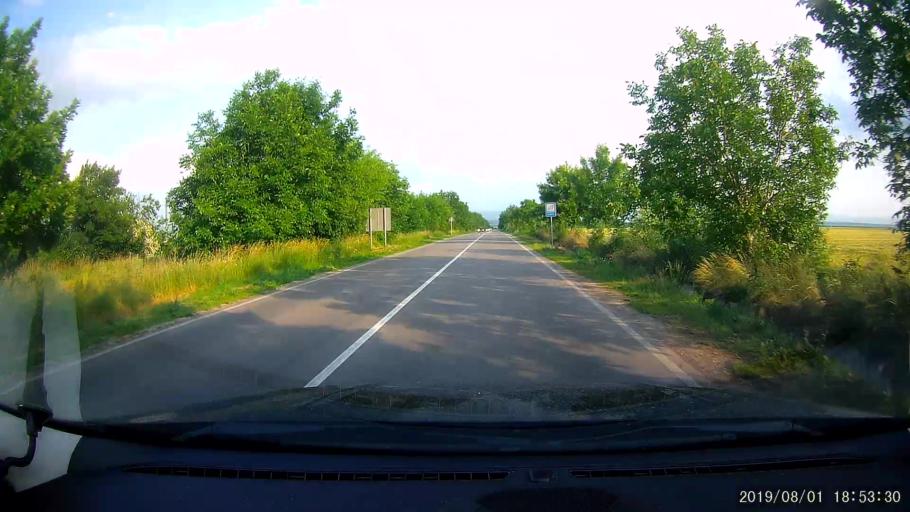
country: BG
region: Shumen
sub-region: Obshtina Shumen
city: Shumen
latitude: 43.2203
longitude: 26.9941
